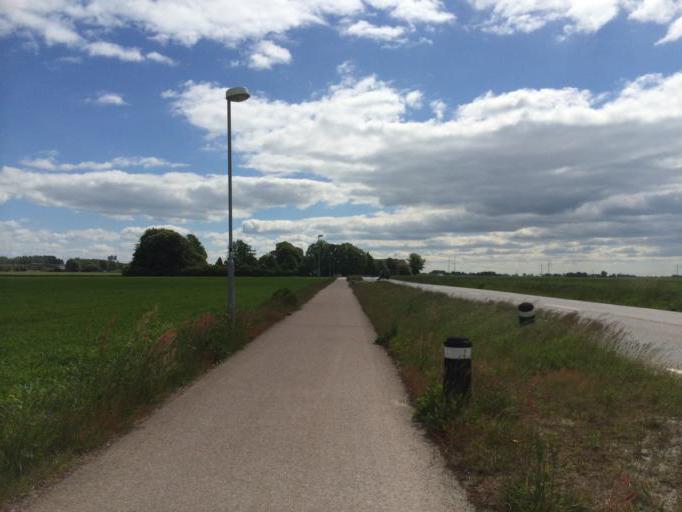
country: SE
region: Skane
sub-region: Staffanstorps Kommun
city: Hjaerup
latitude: 55.6730
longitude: 13.1148
